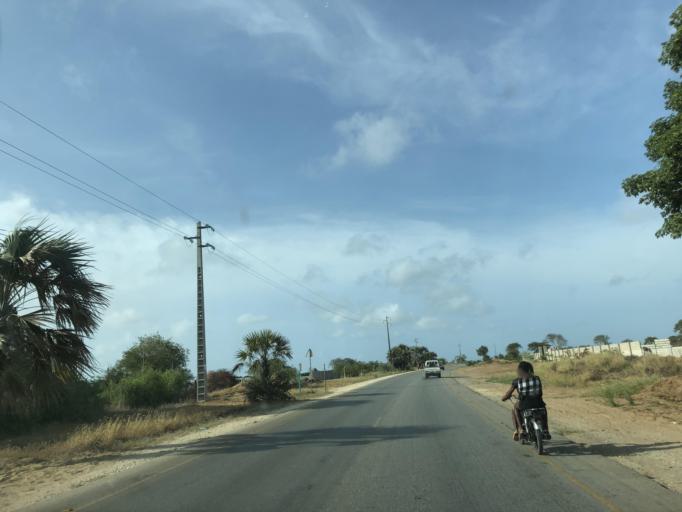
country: AO
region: Luanda
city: Luanda
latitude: -9.0891
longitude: 13.0219
